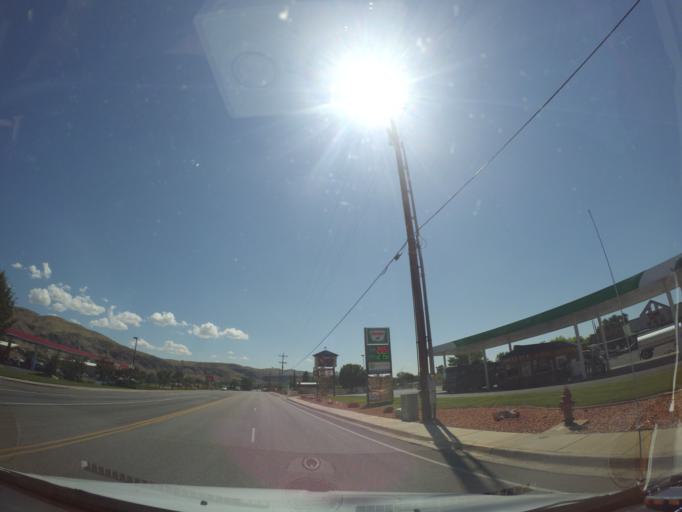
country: US
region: Utah
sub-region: Washington County
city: LaVerkin
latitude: 37.2107
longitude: -113.2722
